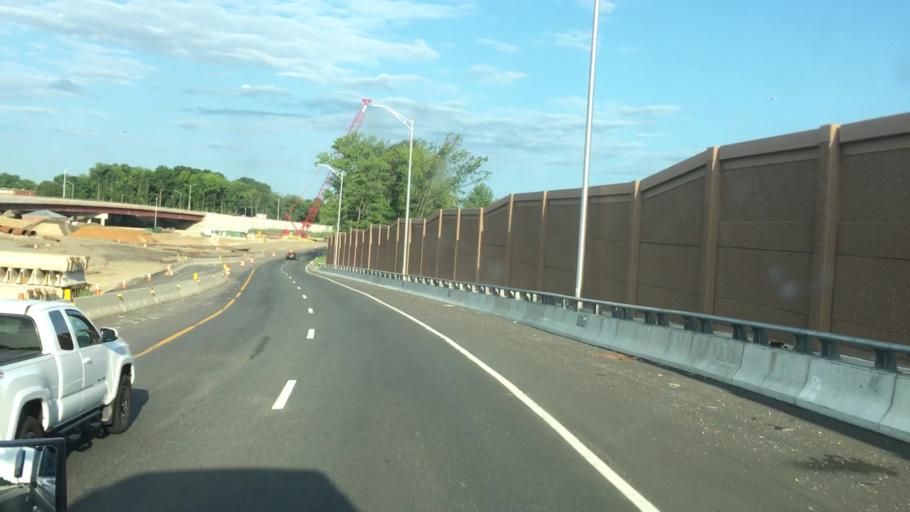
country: US
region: New Jersey
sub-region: Camden County
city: Mount Ephraim
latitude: 39.8752
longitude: -75.0980
